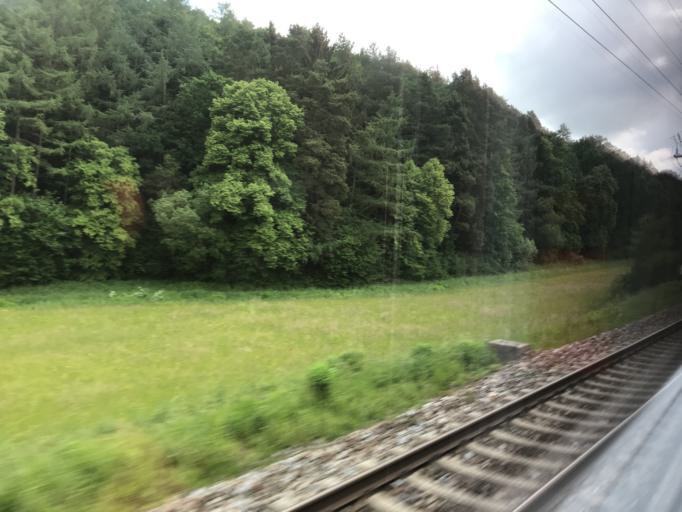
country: DE
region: Bavaria
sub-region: Swabia
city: Landensberg
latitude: 48.3827
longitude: 10.5055
